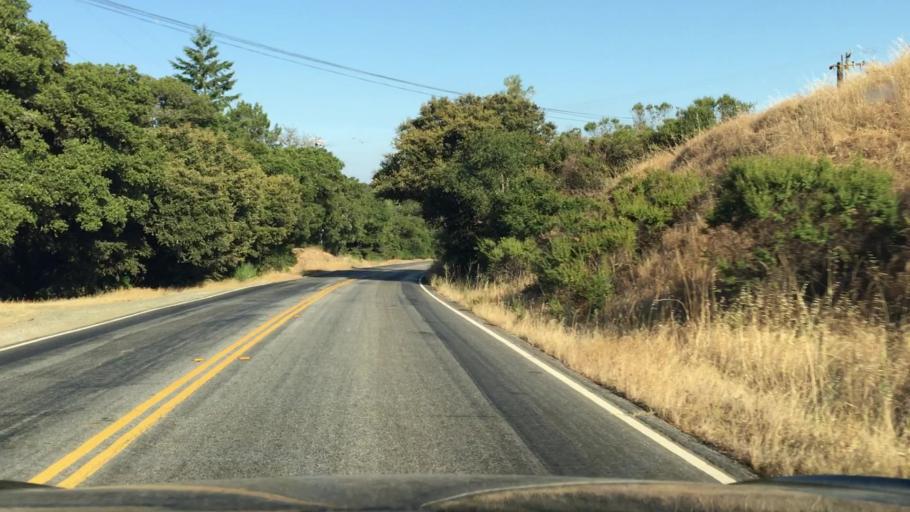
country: US
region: California
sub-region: San Mateo County
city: Portola Valley
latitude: 37.3185
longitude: -122.1918
